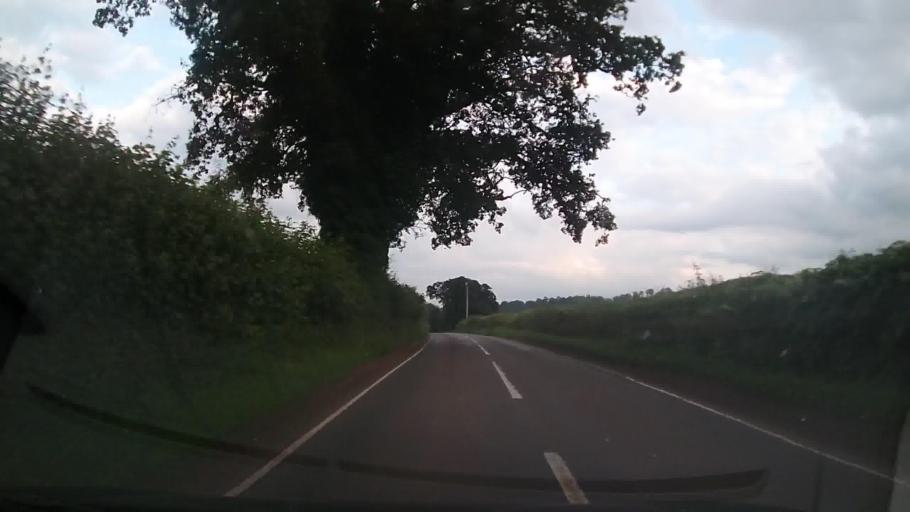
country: GB
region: Wales
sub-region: Sir Powys
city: Llanfechain
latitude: 52.8039
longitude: -3.1374
